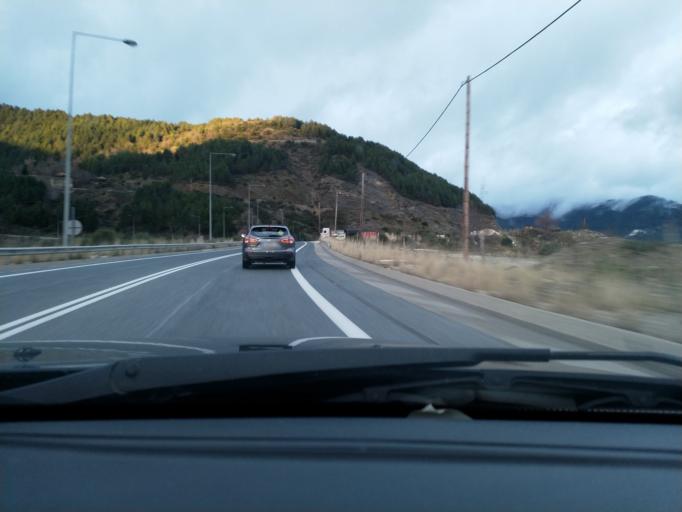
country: GR
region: Epirus
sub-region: Nomos Ioanninon
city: Metsovo
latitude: 39.7622
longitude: 21.1729
